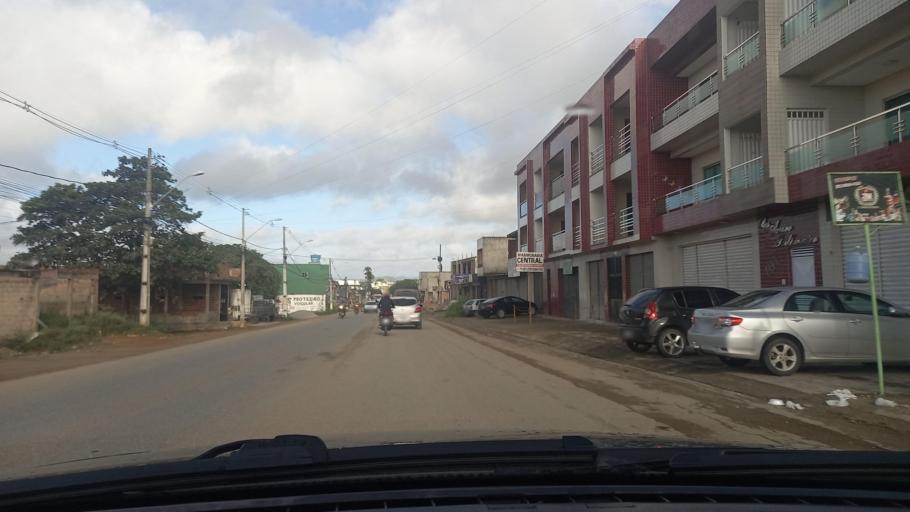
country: BR
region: Pernambuco
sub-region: Vitoria De Santo Antao
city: Vitoria de Santo Antao
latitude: -8.1179
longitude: -35.3157
